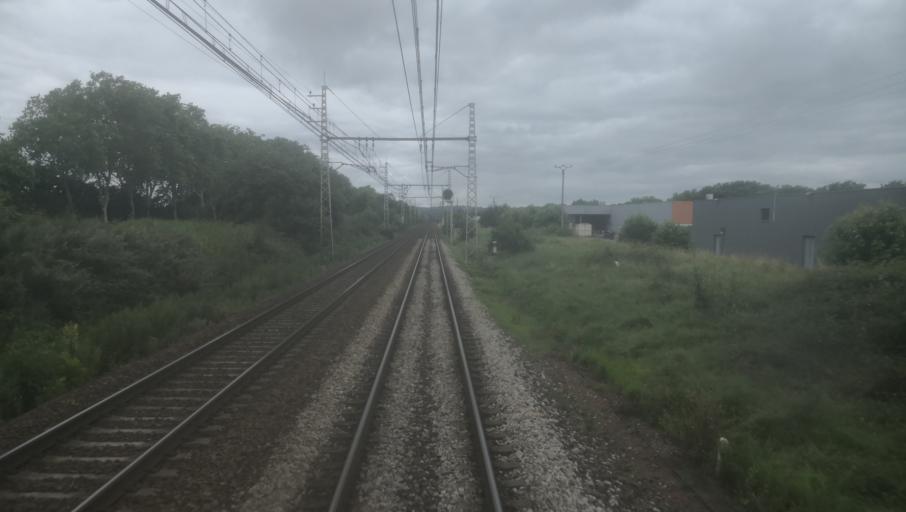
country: FR
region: Midi-Pyrenees
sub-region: Departement de la Haute-Garonne
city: Saint-Jory
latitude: 43.7457
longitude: 1.3653
